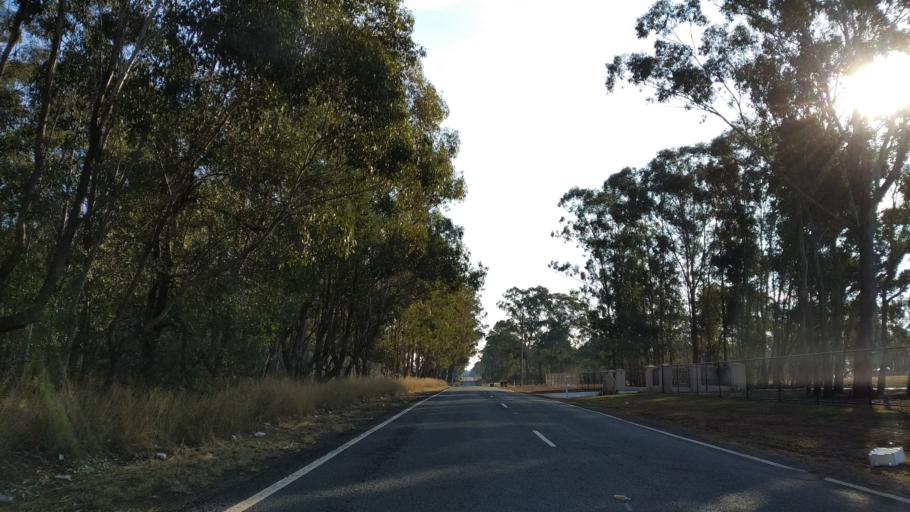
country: AU
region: New South Wales
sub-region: Penrith Municipality
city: Werrington County
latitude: -33.7158
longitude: 150.7511
